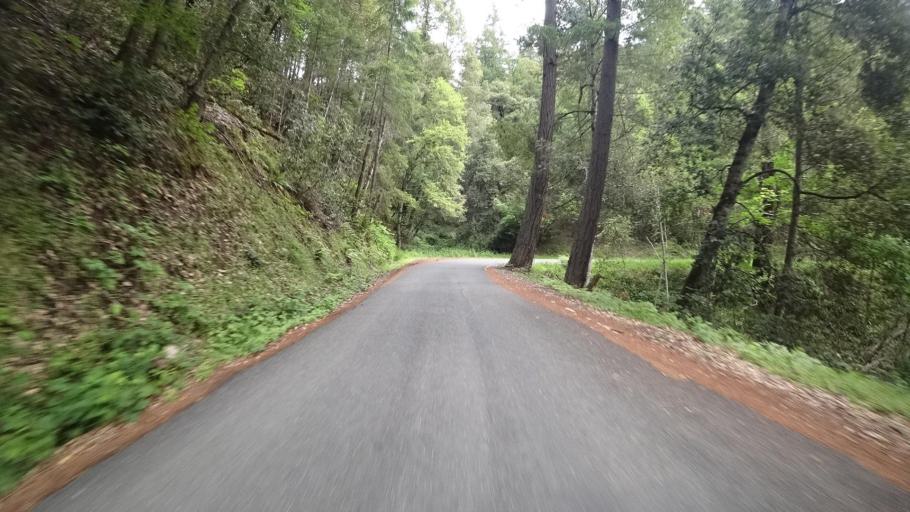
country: US
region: California
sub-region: Humboldt County
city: Willow Creek
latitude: 40.9497
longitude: -123.6196
